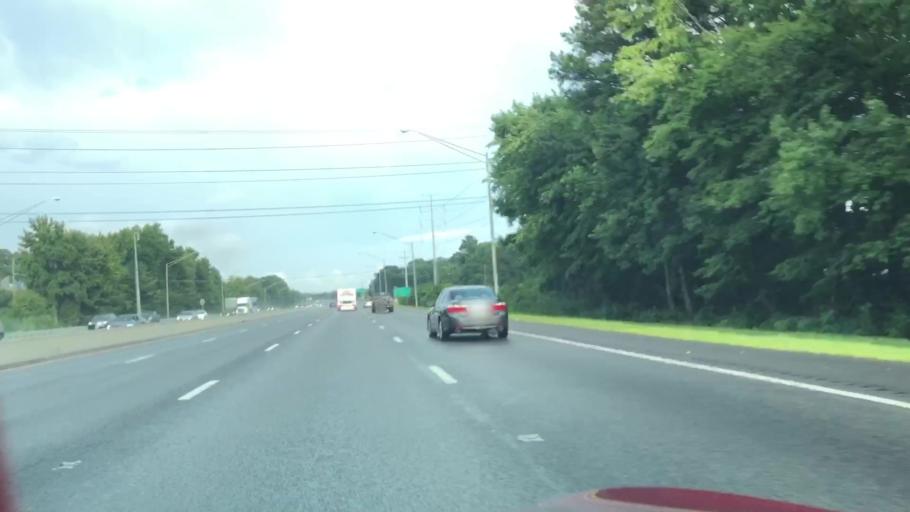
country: US
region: Virginia
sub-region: City of Virginia Beach
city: Virginia Beach
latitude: 36.8369
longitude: -76.0759
